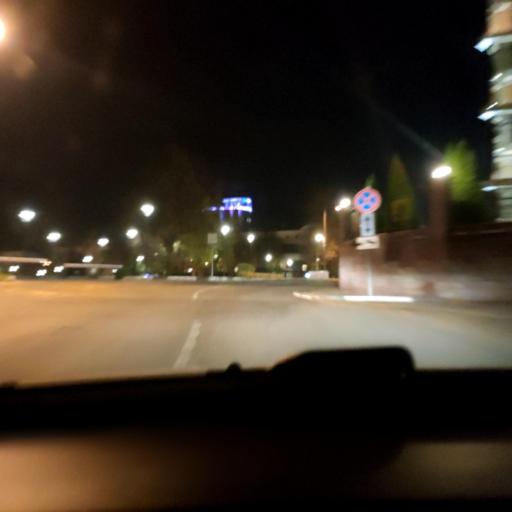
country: RU
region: Voronezj
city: Voronezh
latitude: 51.6666
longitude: 39.2113
